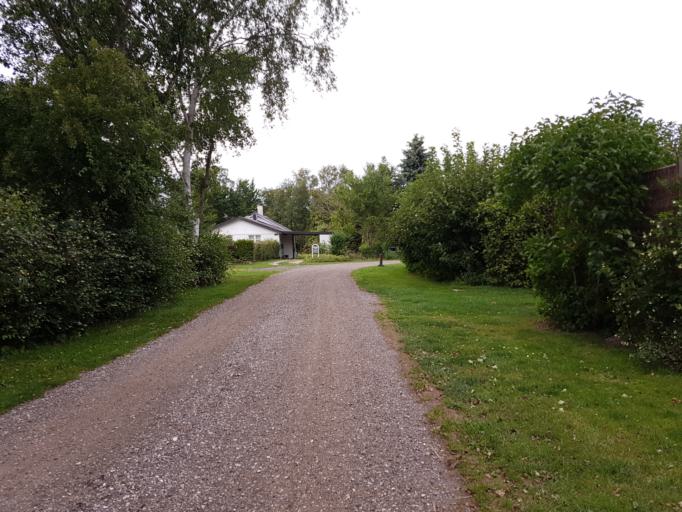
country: DK
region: Zealand
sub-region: Guldborgsund Kommune
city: Nykobing Falster
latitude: 54.5919
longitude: 11.9609
